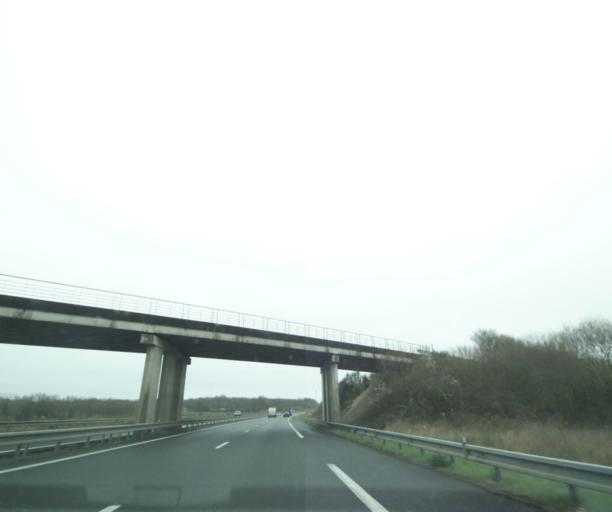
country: FR
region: Centre
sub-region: Departement du Loir-et-Cher
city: Nouan-le-Fuzelier
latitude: 47.5119
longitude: 2.0090
